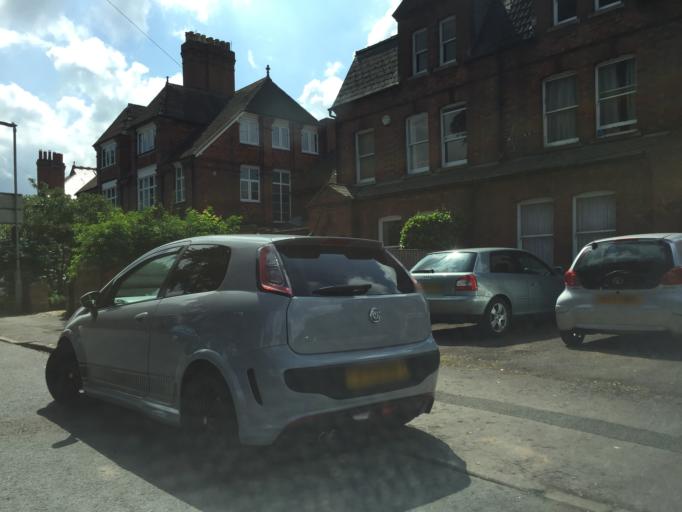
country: GB
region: England
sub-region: Gloucestershire
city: Gloucester
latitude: 51.8715
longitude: -2.2345
